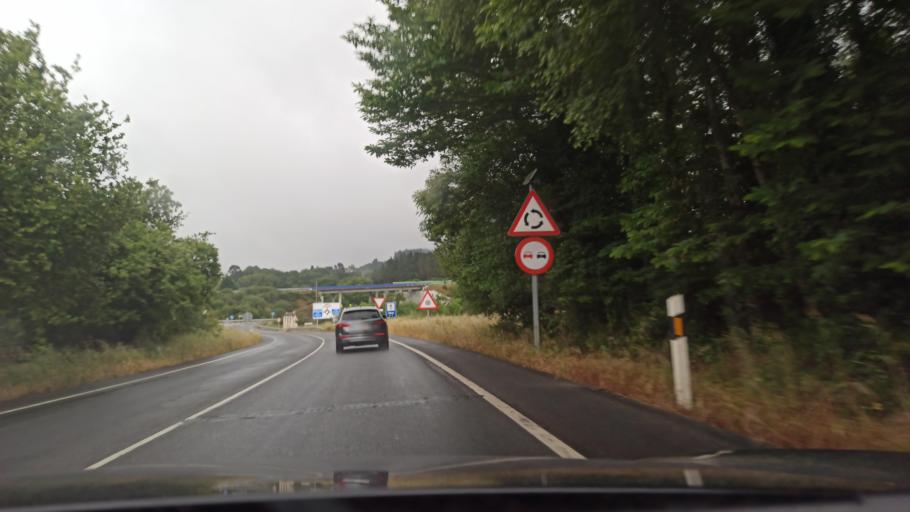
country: ES
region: Galicia
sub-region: Provincia de Lugo
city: Ourol
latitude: 42.9407
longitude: -7.6292
